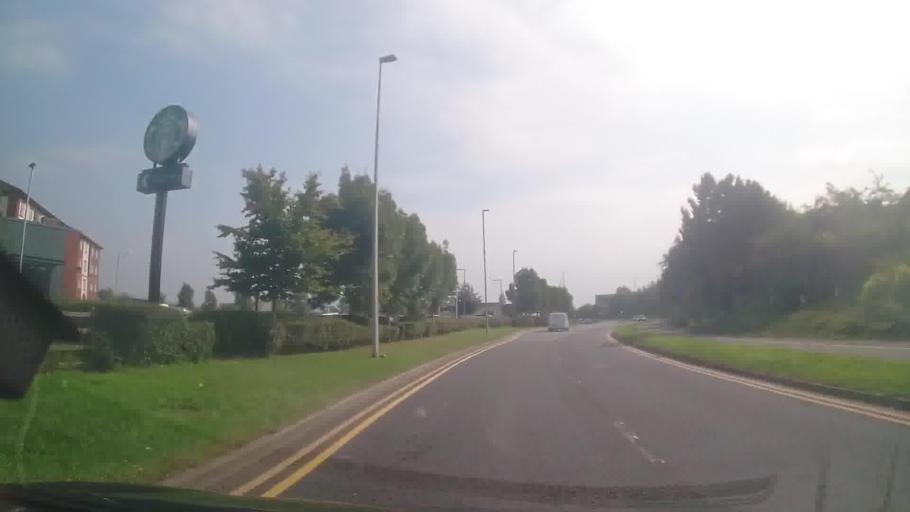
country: GB
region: England
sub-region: Warrington
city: Burtonwood
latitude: 53.4155
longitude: -2.6406
